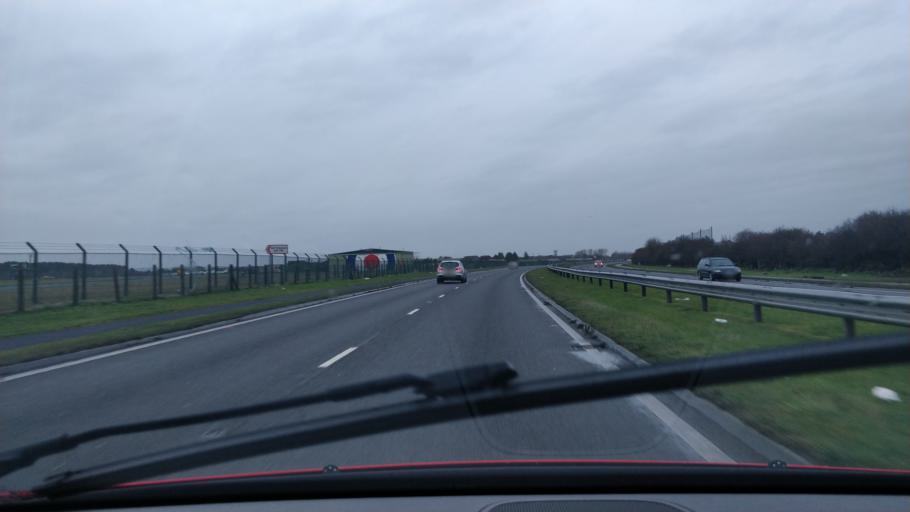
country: GB
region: England
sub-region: Sefton
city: Formby
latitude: 53.5789
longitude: -3.0501
